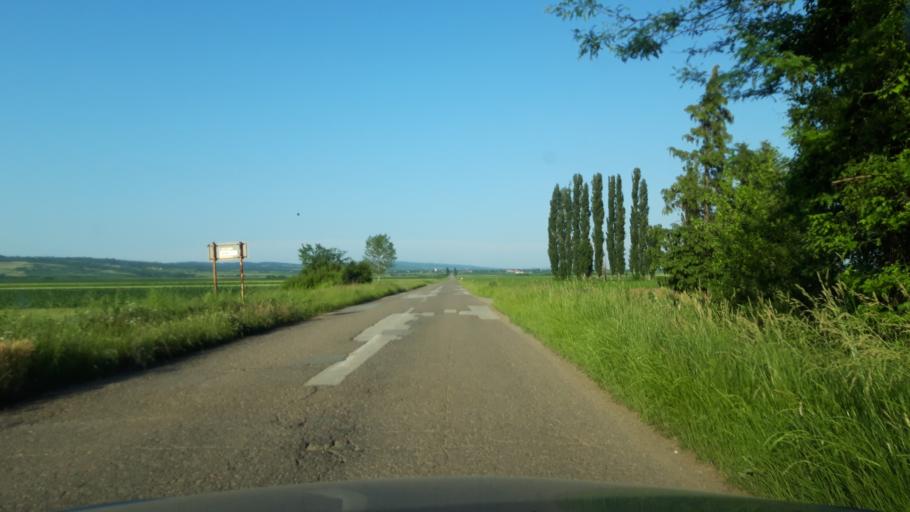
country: HR
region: Vukovarsko-Srijemska
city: Ilok
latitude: 45.1014
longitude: 19.4569
